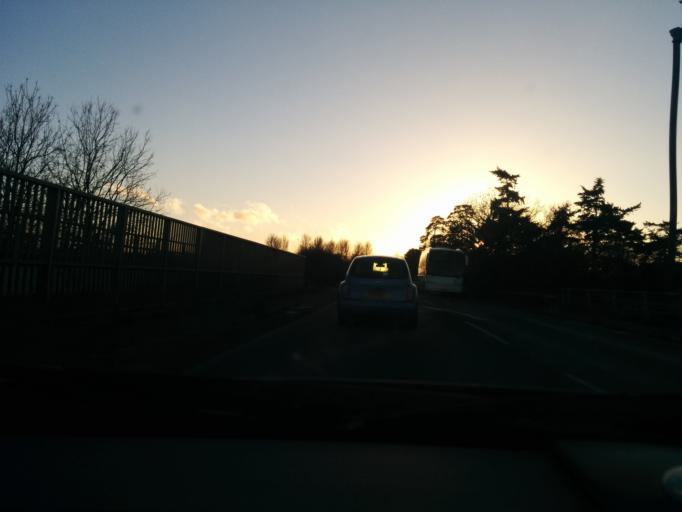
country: GB
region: England
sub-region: Buckinghamshire
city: Denham
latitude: 51.5471
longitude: -0.5158
